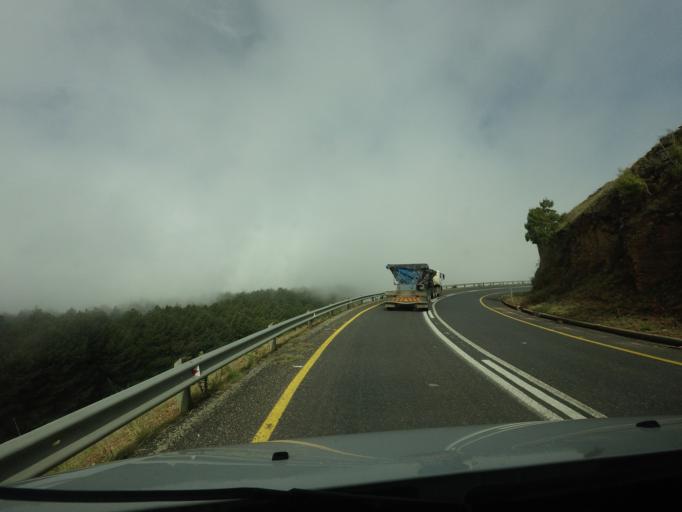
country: ZA
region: Mpumalanga
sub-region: Ehlanzeni District
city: Lydenburg
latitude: -25.1587
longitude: 30.6296
